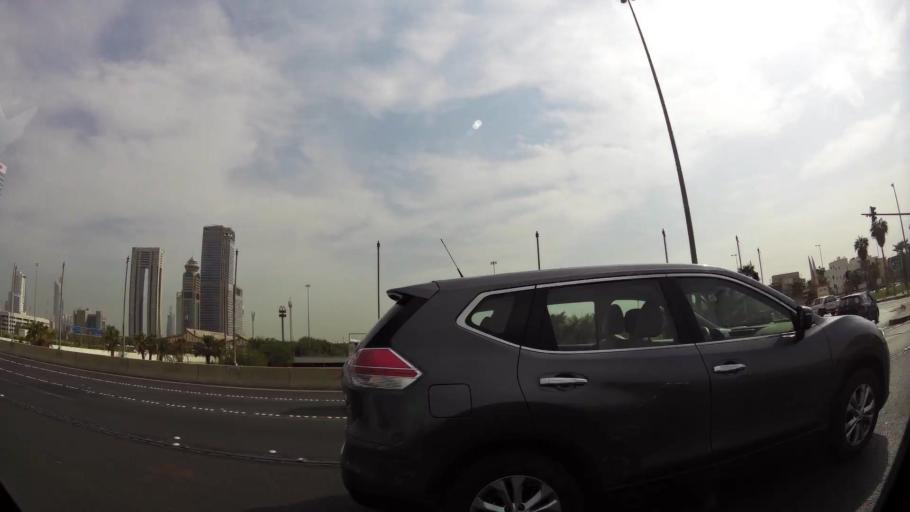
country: KW
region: Al Asimah
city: Kuwait City
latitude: 29.3586
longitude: 47.9736
